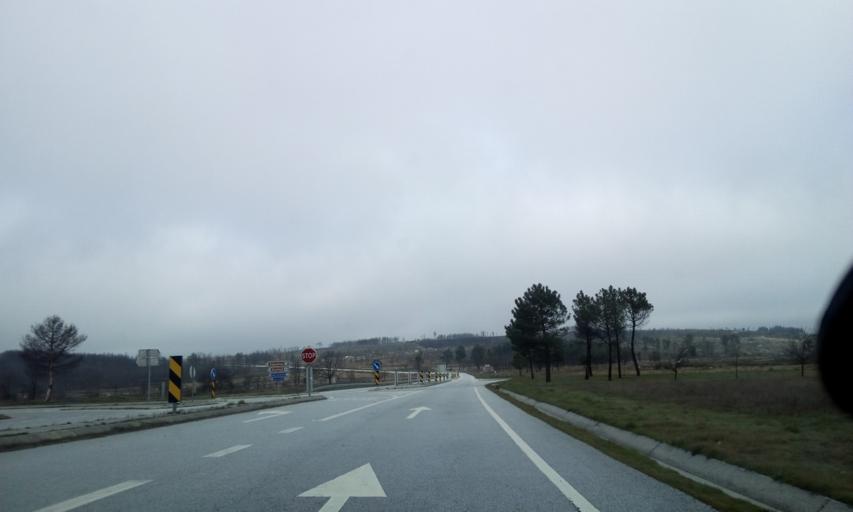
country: PT
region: Guarda
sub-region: Fornos de Algodres
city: Fornos de Algodres
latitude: 40.6939
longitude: -7.4733
